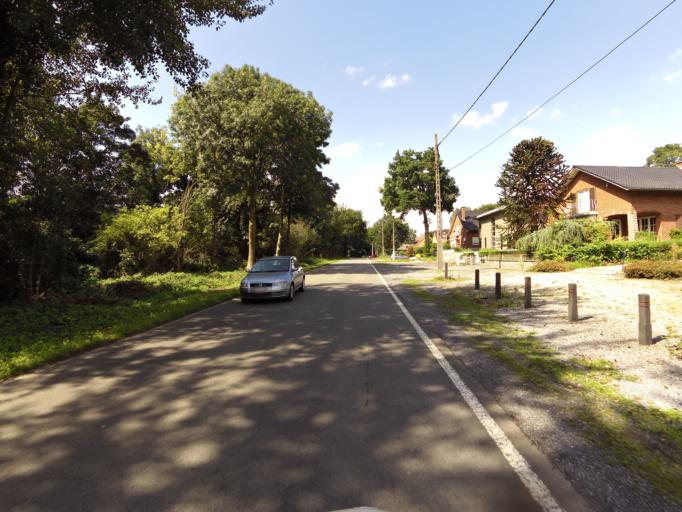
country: BE
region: Wallonia
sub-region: Province du Hainaut
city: Saint-Ghislain
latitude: 50.4854
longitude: 3.8279
